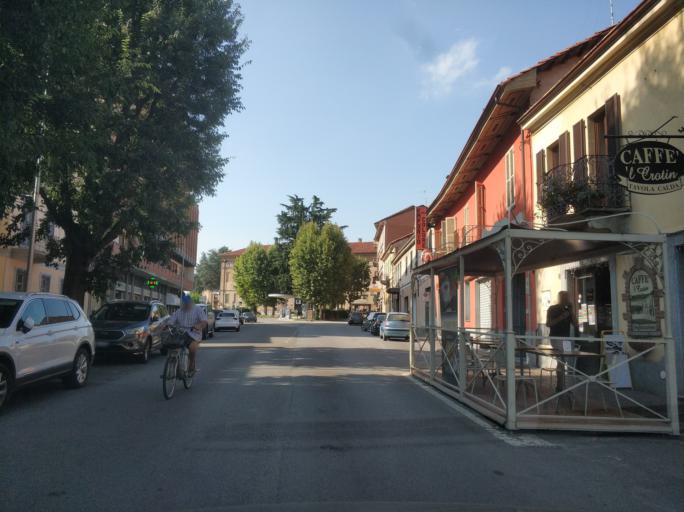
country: IT
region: Piedmont
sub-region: Provincia di Cuneo
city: Bra
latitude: 44.7007
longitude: 7.8483
